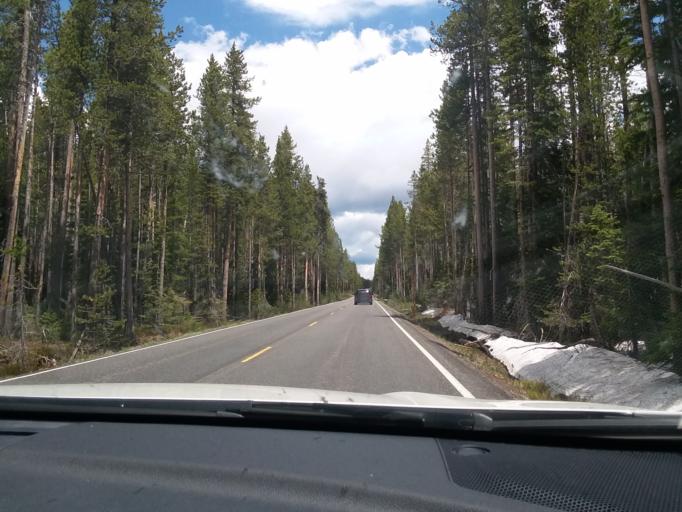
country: US
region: Idaho
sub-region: Teton County
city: Driggs
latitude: 44.1798
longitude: -110.6600
